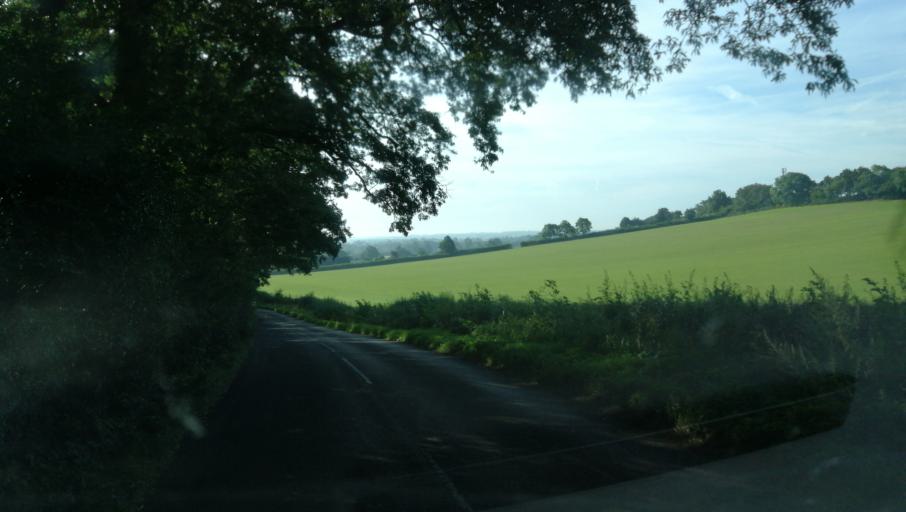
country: GB
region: England
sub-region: Oxfordshire
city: Bloxham
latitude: 52.0270
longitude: -1.4022
